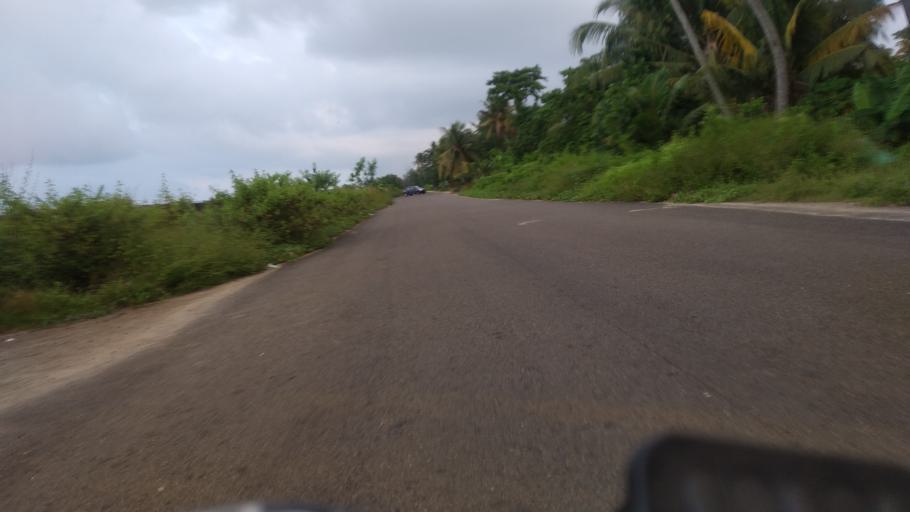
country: IN
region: Kerala
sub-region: Ernakulam
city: Cochin
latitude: 10.0021
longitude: 76.2197
